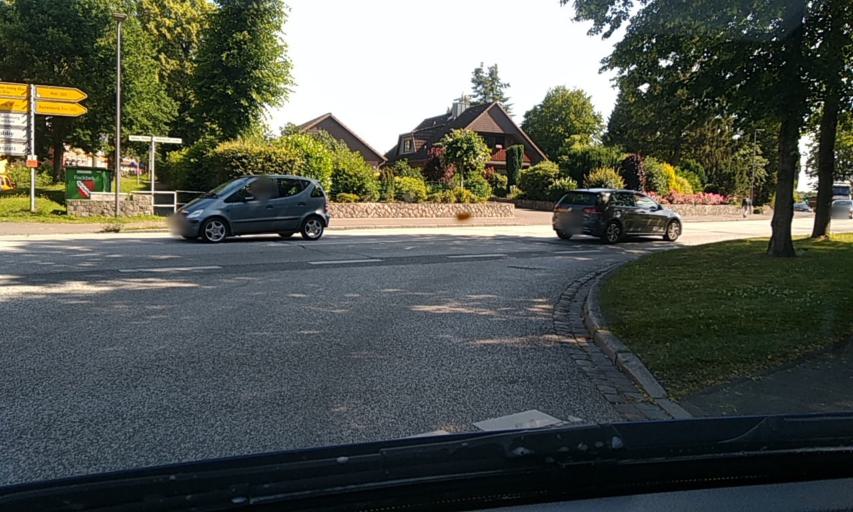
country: DE
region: Schleswig-Holstein
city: Fockbek
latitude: 54.3033
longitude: 9.5998
